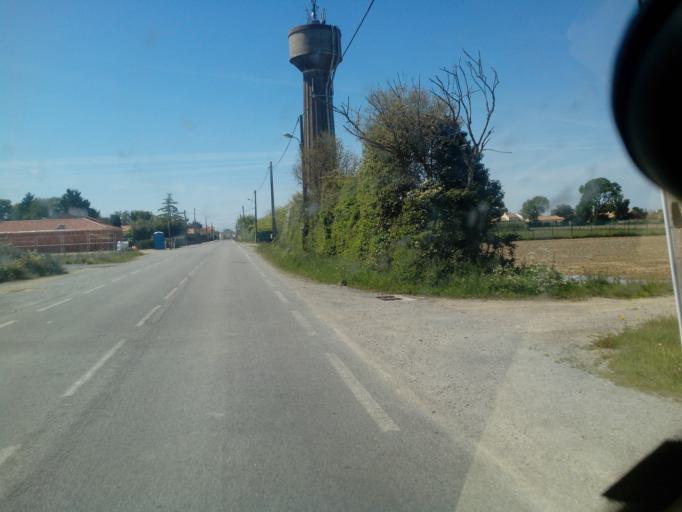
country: FR
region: Pays de la Loire
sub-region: Departement de la Loire-Atlantique
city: Pornic
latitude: 47.1080
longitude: -2.0812
